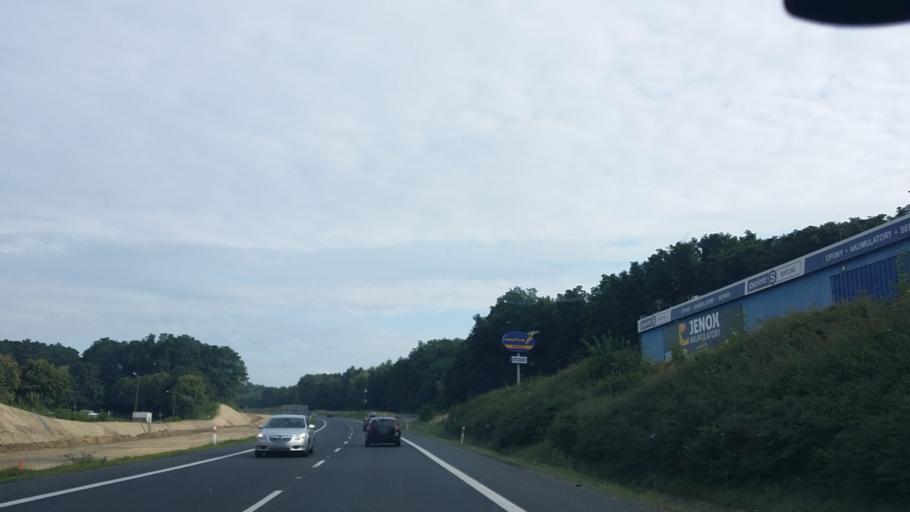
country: PL
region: Lubusz
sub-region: Zielona Gora
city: Zielona Gora
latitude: 51.9380
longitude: 15.5482
